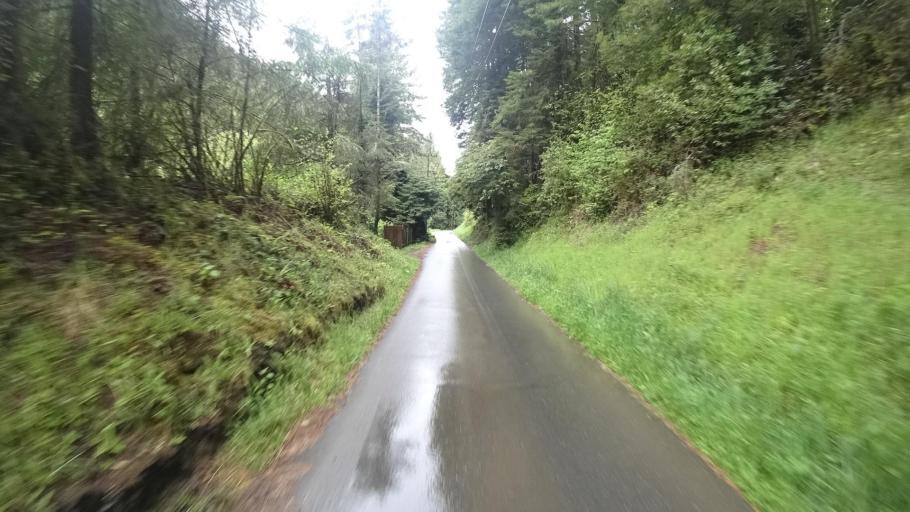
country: US
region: California
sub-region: Humboldt County
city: Bayside
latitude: 40.8159
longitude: -124.0277
